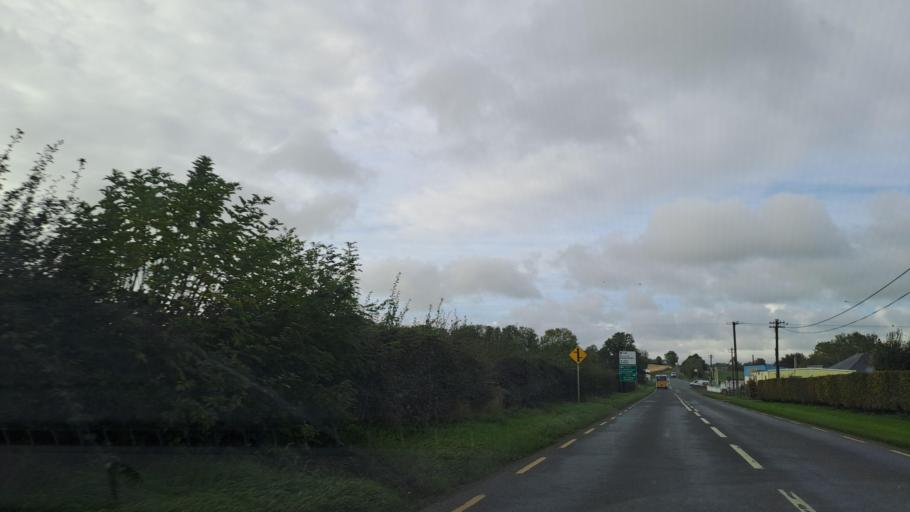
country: IE
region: Leinster
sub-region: An Mhi
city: Navan
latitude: 53.7851
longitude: -6.7321
